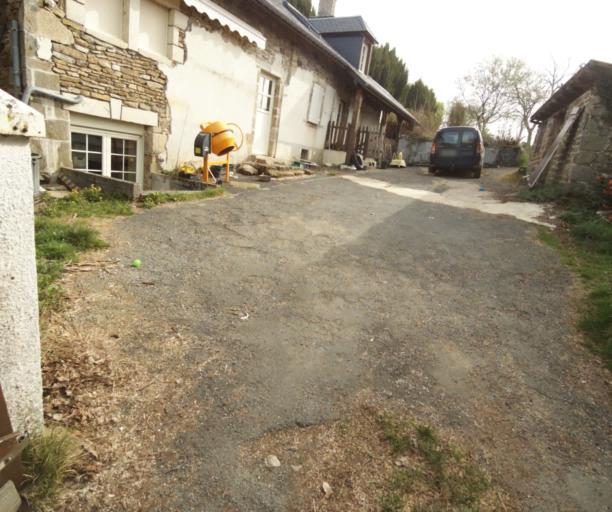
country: FR
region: Limousin
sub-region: Departement de la Correze
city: Correze
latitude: 45.4104
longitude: 1.8028
